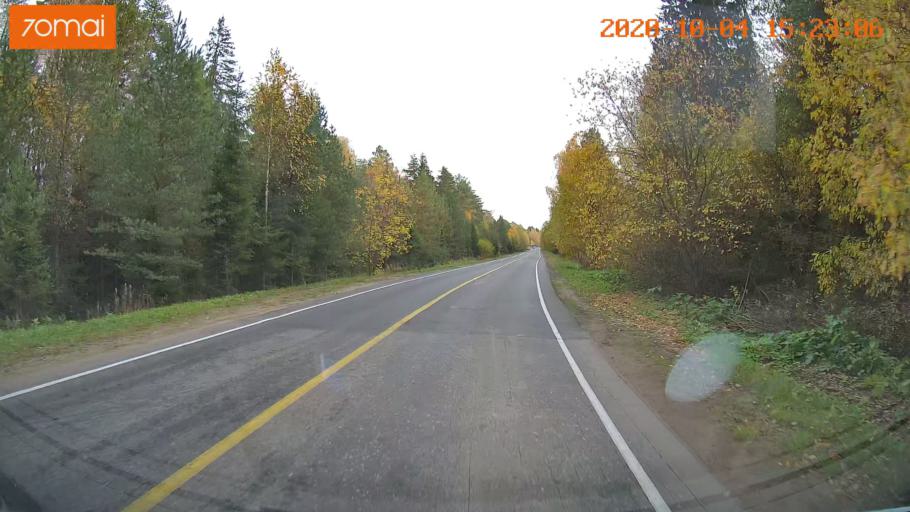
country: RU
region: Ivanovo
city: Bogorodskoye
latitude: 57.0767
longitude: 40.9454
